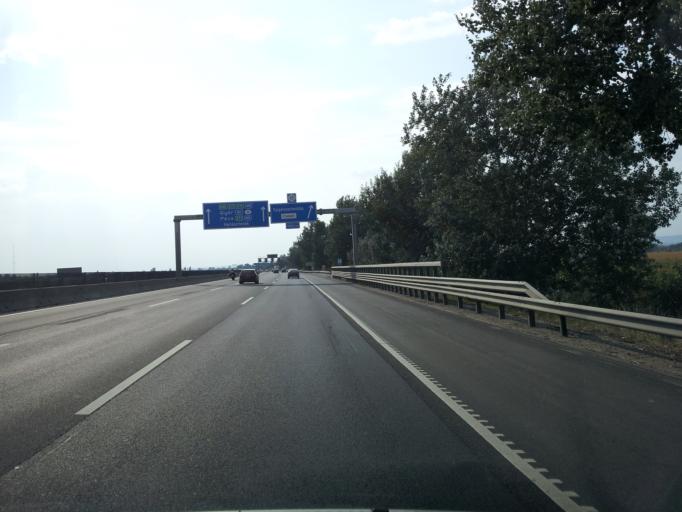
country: HU
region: Pest
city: Dunaharaszti
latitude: 47.3769
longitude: 19.0755
